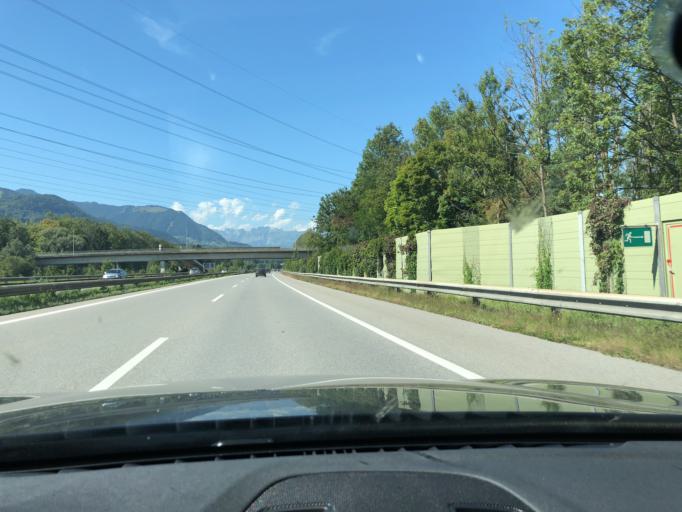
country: AT
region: Vorarlberg
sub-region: Politischer Bezirk Feldkirch
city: Schlins
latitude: 47.1969
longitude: 9.6943
